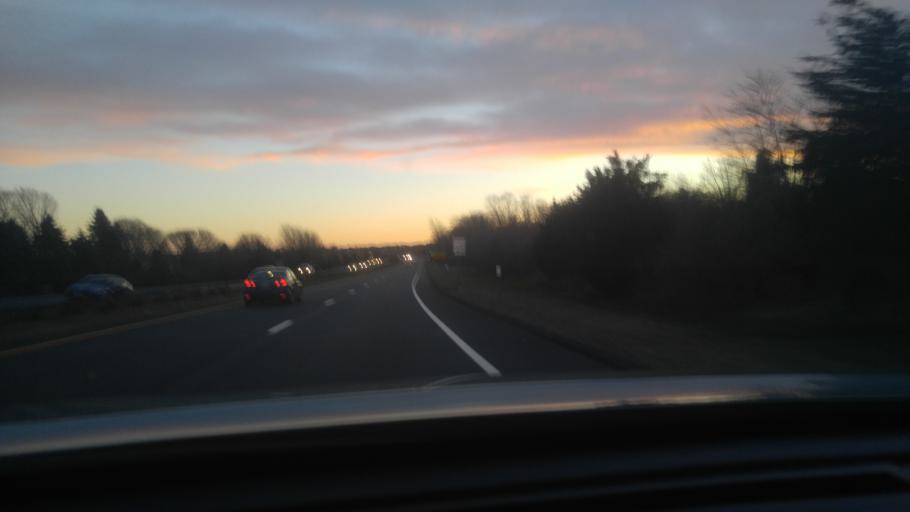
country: US
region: Rhode Island
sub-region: Newport County
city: Jamestown
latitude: 41.5189
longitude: -71.3665
